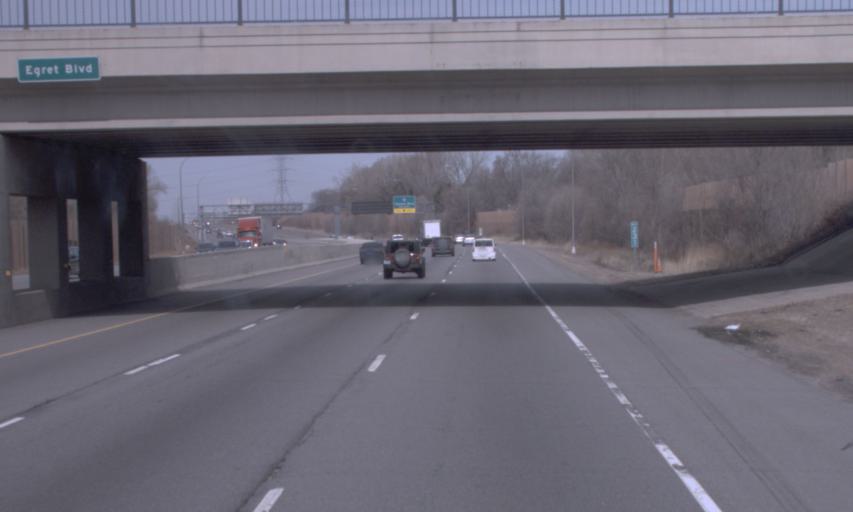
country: US
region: Minnesota
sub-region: Anoka County
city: Coon Rapids
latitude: 45.1629
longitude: -93.2848
